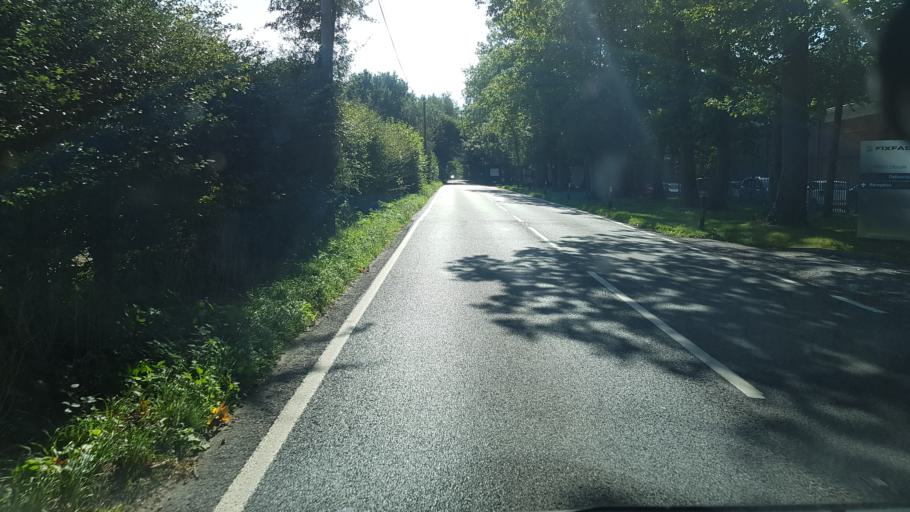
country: GB
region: England
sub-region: Kent
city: Borough Green
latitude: 51.2795
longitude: 0.3526
